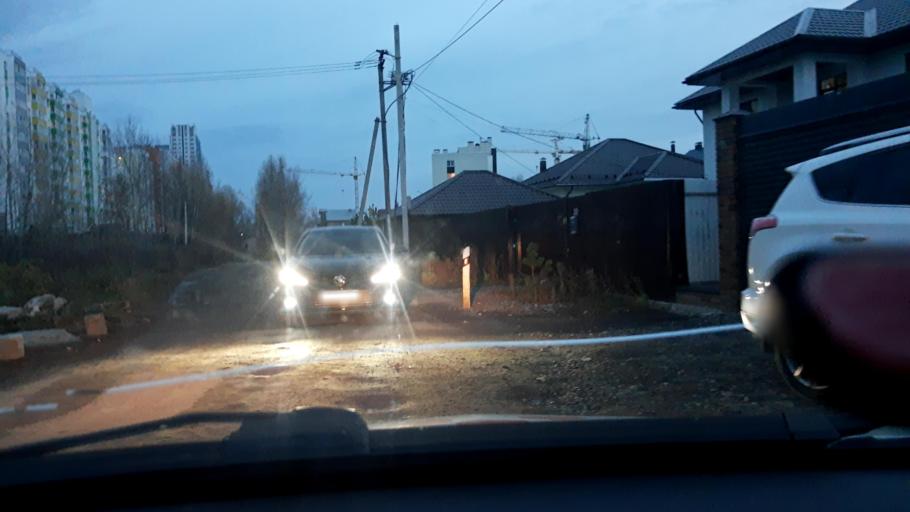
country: RU
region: Bashkortostan
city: Ufa
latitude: 54.6864
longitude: 55.9784
